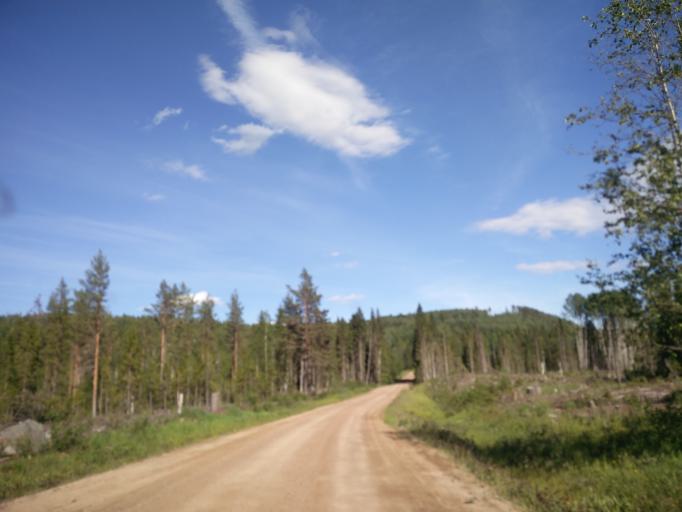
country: SE
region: Vaesternorrland
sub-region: Ange Kommun
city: Fransta
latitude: 62.2043
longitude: 16.3520
